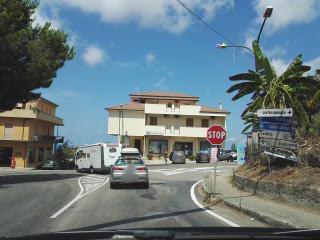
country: IT
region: Calabria
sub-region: Provincia di Vibo-Valentia
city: Ricadi
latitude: 38.6256
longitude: 15.8646
